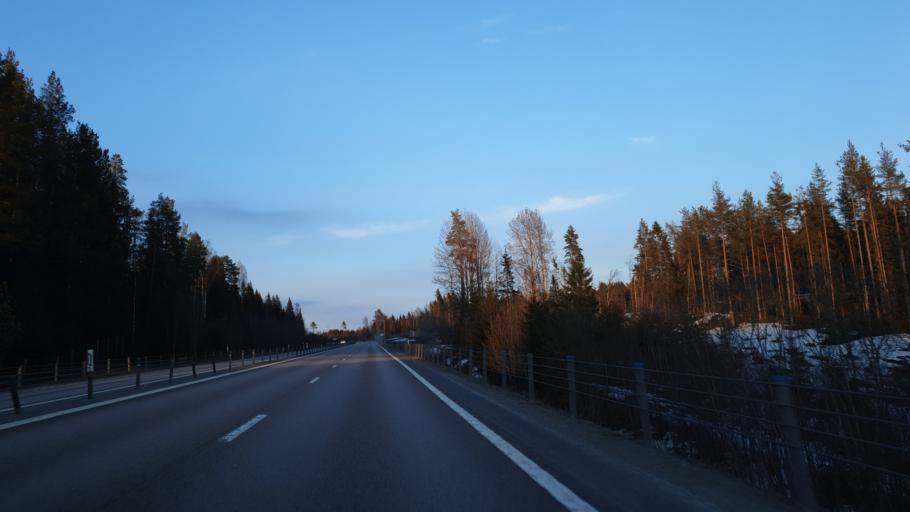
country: SE
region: Vaesternorrland
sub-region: Timra Kommun
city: Soraker
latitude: 62.5623
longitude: 17.7184
